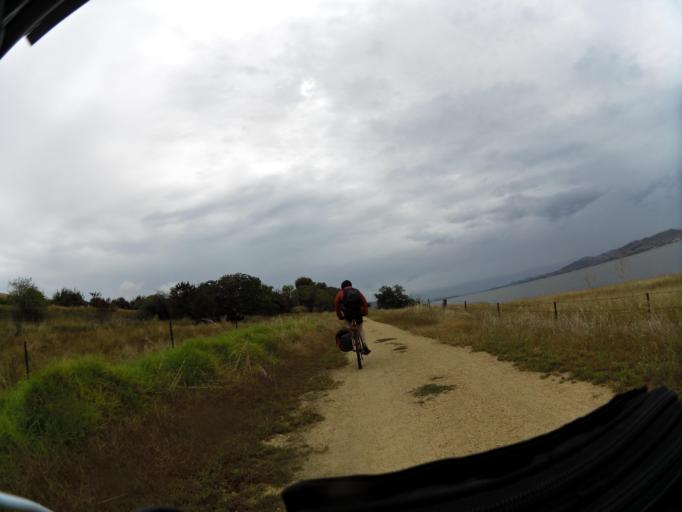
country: AU
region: New South Wales
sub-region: Albury Municipality
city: East Albury
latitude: -36.2234
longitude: 147.0736
